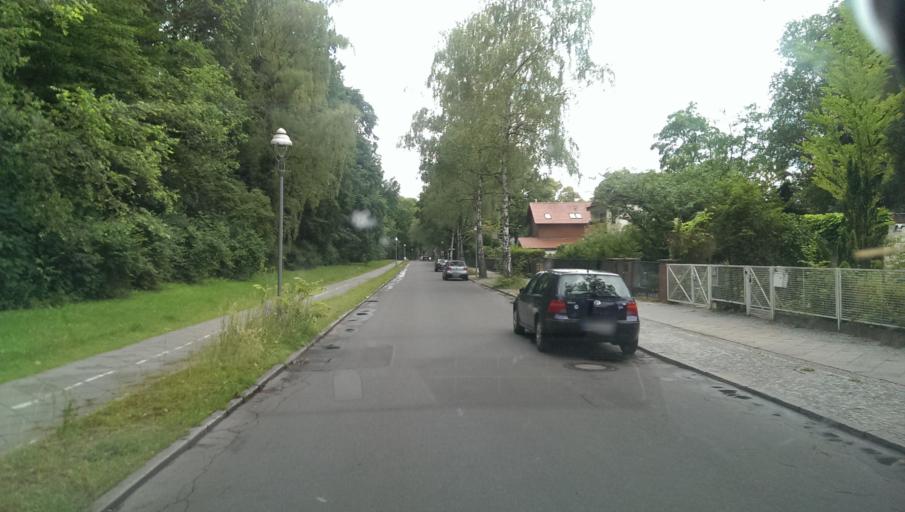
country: DE
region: Brandenburg
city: Teltow
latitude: 52.4228
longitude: 13.2695
